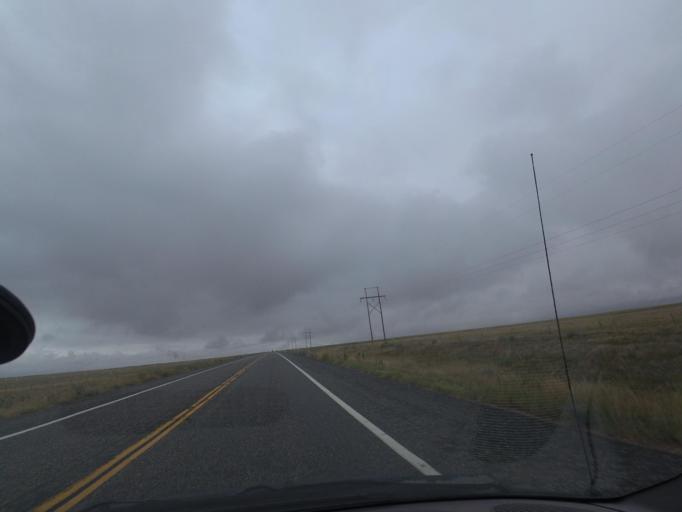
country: US
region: Colorado
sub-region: Washington County
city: Akron
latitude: 39.7397
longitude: -103.4856
